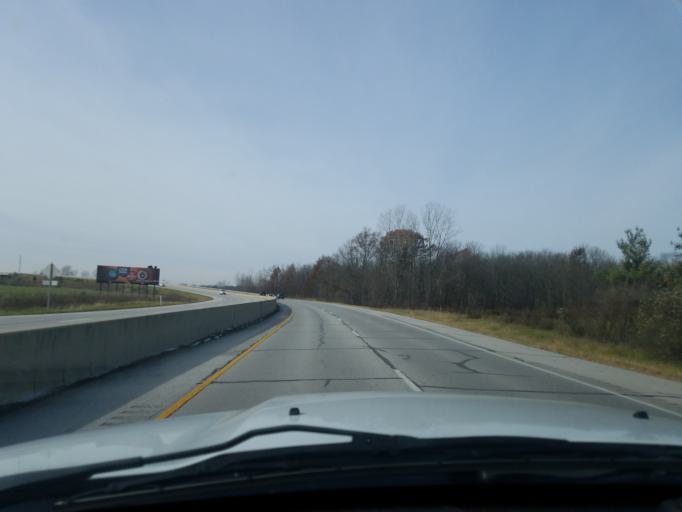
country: US
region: Indiana
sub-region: Delaware County
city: Yorktown
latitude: 40.2215
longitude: -85.5221
